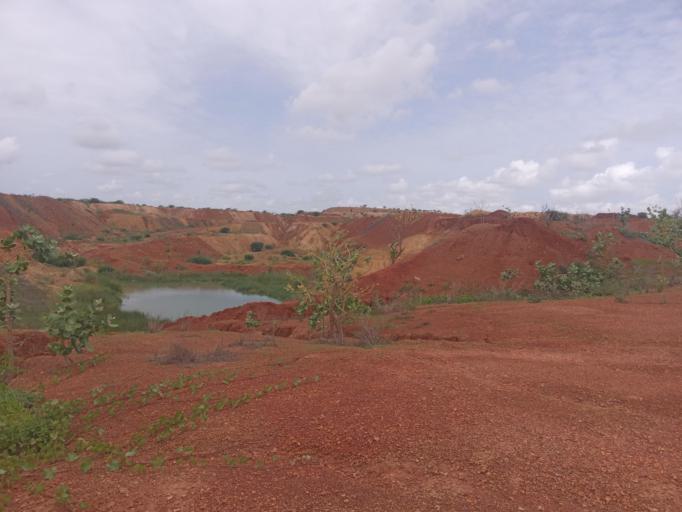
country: SN
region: Thies
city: Thies Nones
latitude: 14.8947
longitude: -16.8777
